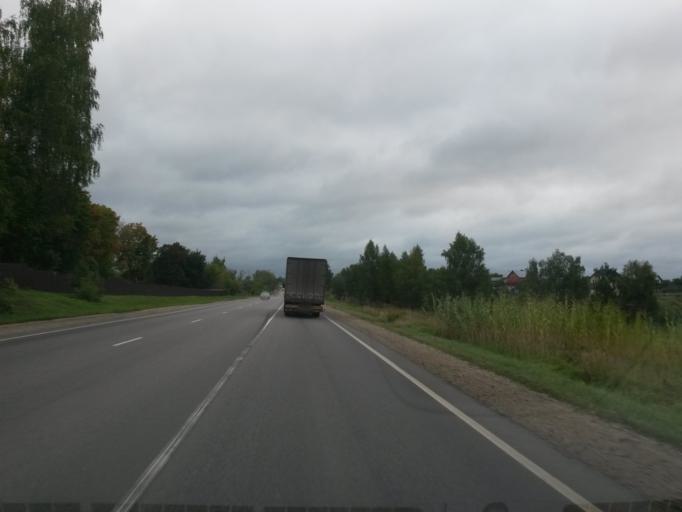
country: RU
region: Moskovskaya
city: Barybino
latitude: 55.2667
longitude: 37.8289
